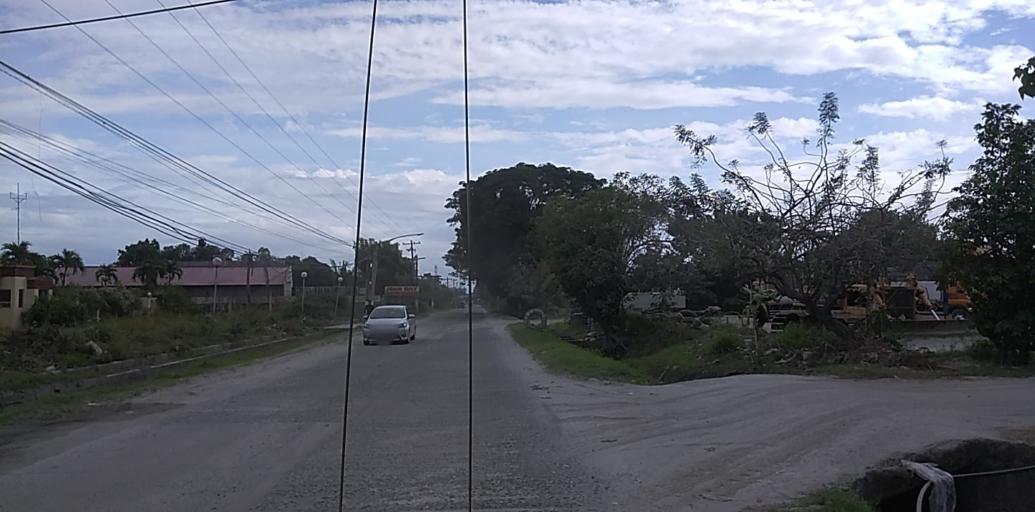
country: PH
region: Central Luzon
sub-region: Province of Pampanga
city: Pulung Santol
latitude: 15.0375
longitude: 120.5643
